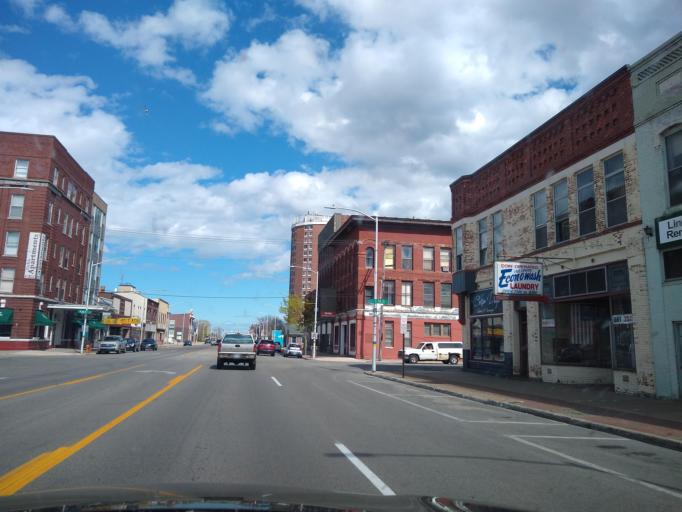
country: US
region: Michigan
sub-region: Delta County
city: Escanaba
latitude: 45.7457
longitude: -87.0574
